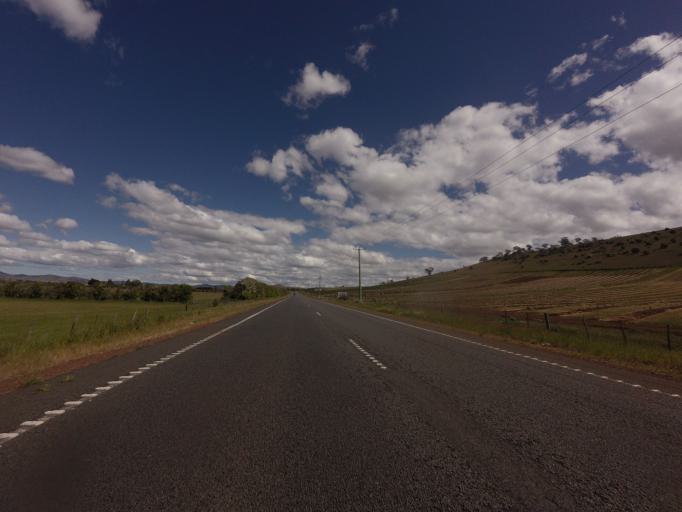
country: AU
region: Tasmania
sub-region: Northern Midlands
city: Evandale
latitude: -42.0518
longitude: 147.4822
